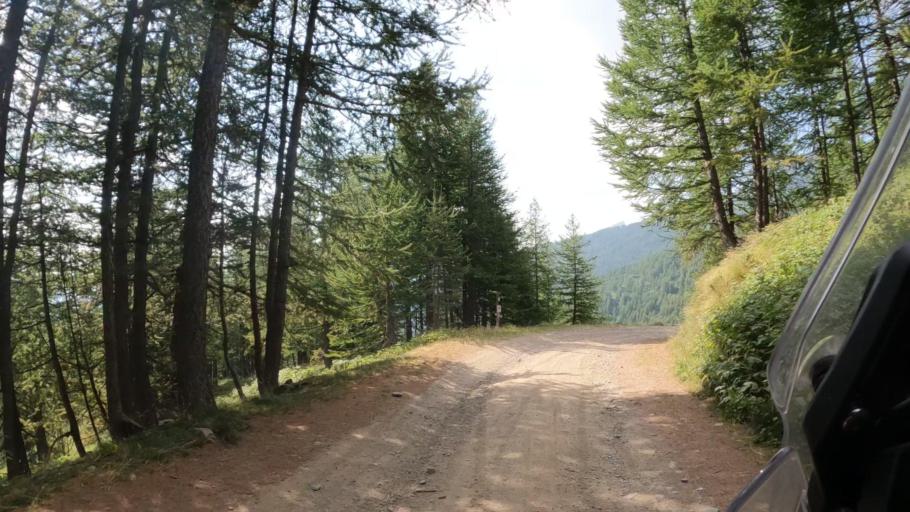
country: IT
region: Piedmont
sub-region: Provincia di Cuneo
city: Briga Alta
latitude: 44.1380
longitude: 7.6771
